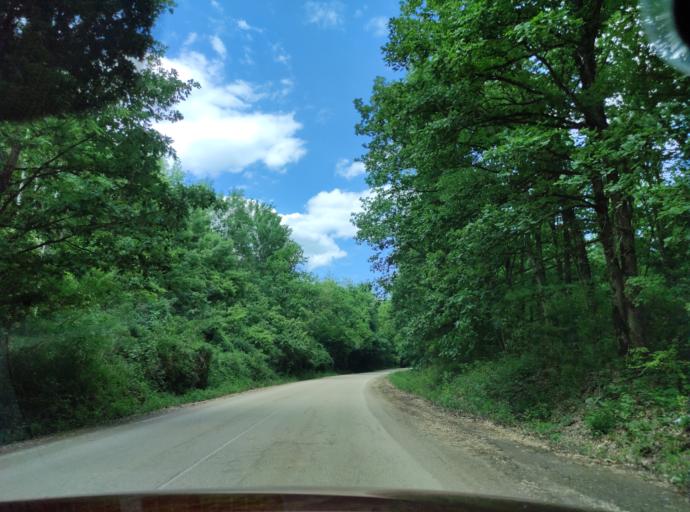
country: BG
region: Montana
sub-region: Obshtina Berkovitsa
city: Berkovitsa
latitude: 43.3768
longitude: 23.0761
